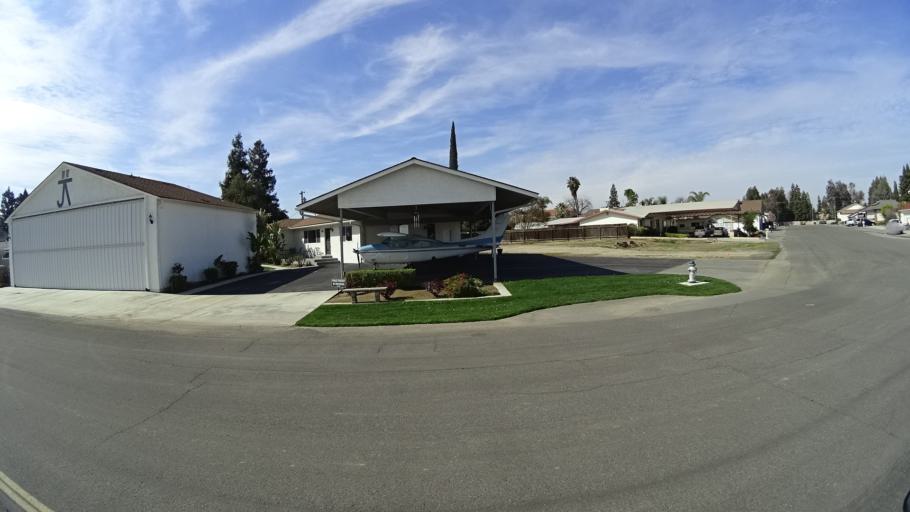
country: US
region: California
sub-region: Fresno County
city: West Park
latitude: 36.8409
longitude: -119.8724
